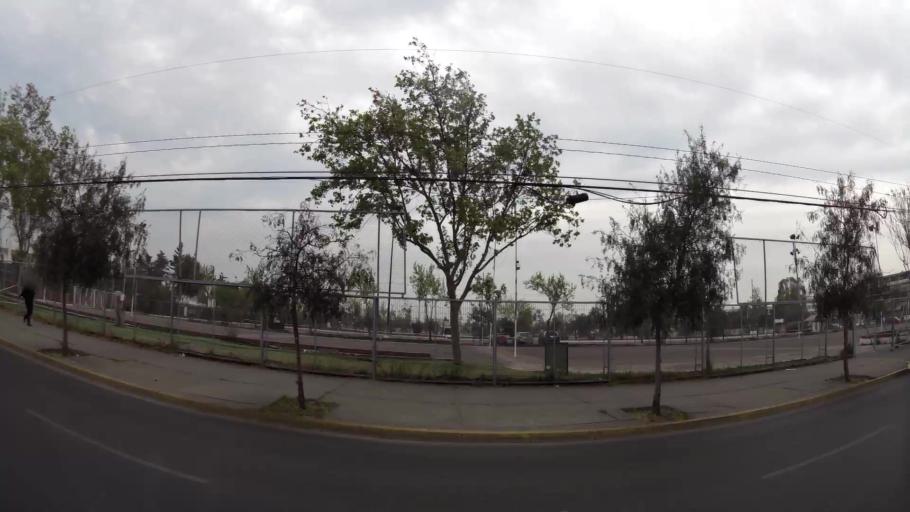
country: CL
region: Santiago Metropolitan
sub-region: Provincia de Santiago
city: Villa Presidente Frei, Nunoa, Santiago, Chile
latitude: -33.4619
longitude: -70.6137
